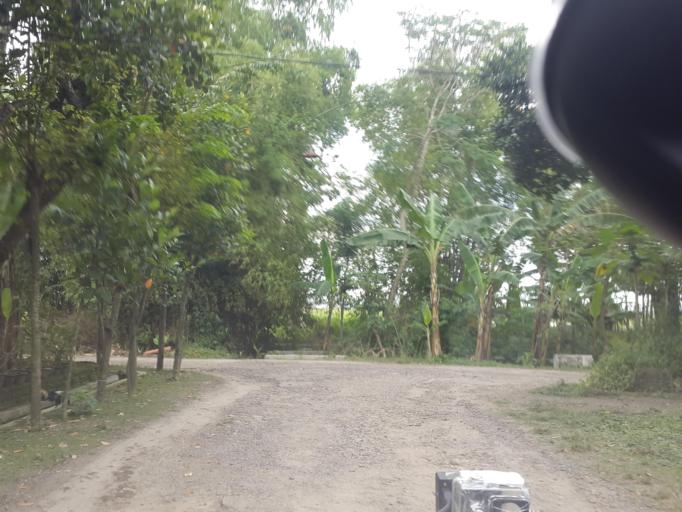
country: ID
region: East Java
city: Madiun
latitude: -7.5656
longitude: 111.6182
